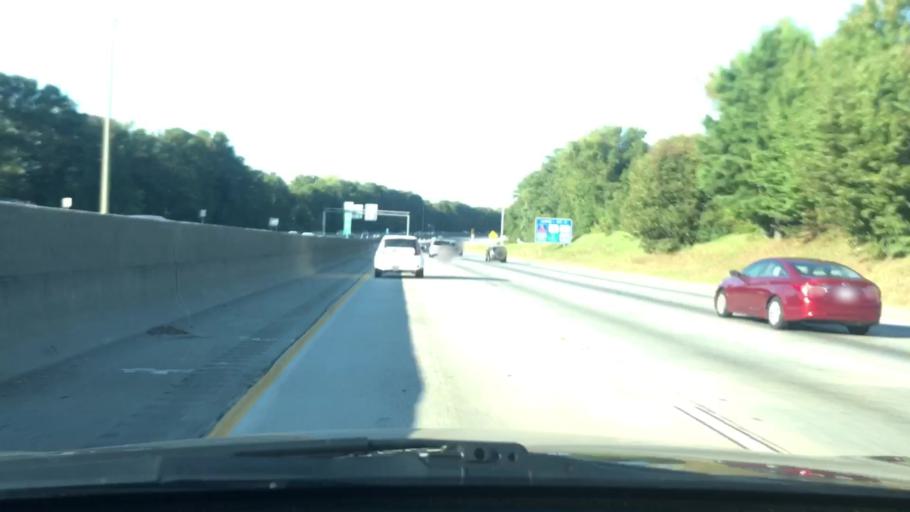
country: US
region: Georgia
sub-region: DeKalb County
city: Clarkston
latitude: 33.8281
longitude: -84.2530
